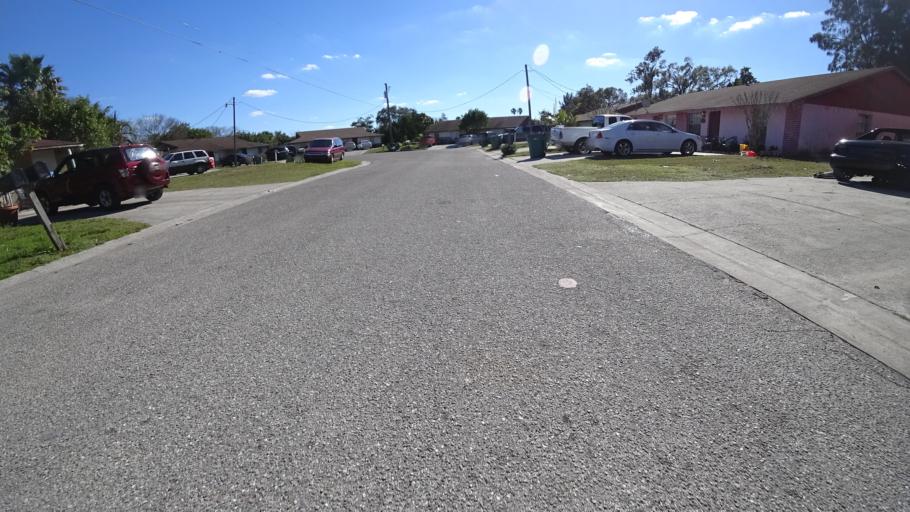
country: US
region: Florida
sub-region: Manatee County
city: Whitfield
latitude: 27.4359
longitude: -82.5484
